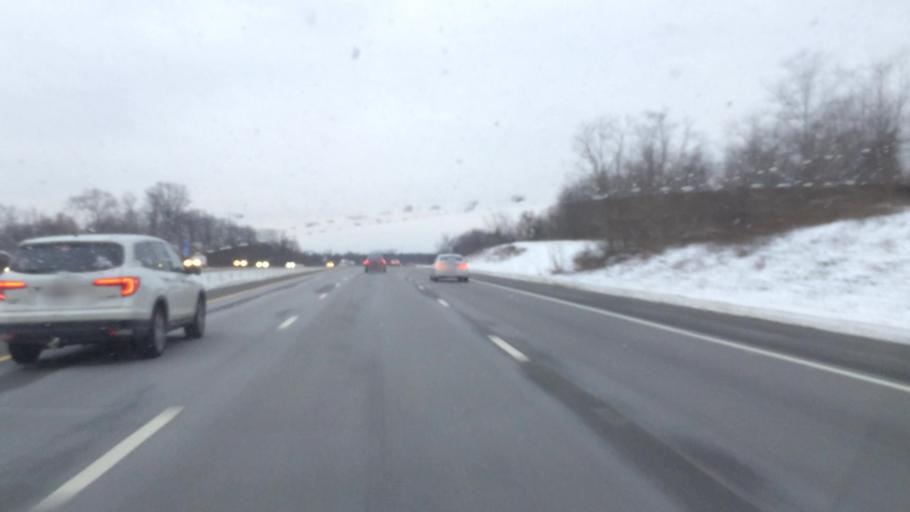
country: US
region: Ohio
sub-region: Medina County
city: Medina
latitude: 41.1723
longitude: -81.7865
